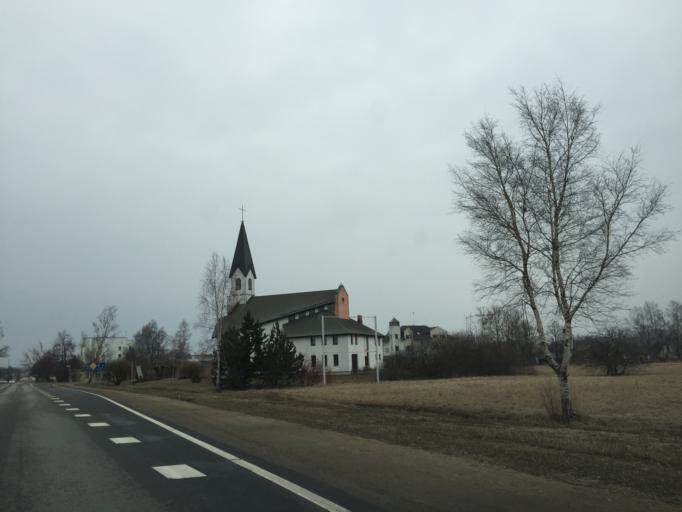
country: LV
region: Salacgrivas
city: Salacgriva
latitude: 57.7482
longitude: 24.3587
